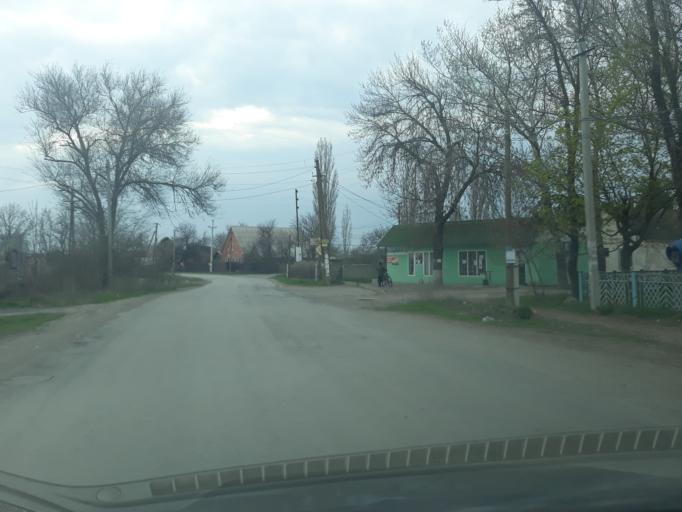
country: RU
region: Rostov
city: Novobessergenovka
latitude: 47.1588
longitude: 38.7050
